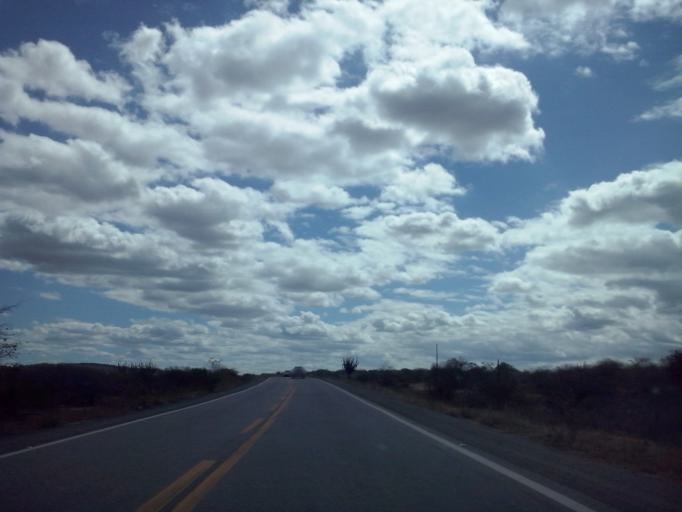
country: BR
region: Paraiba
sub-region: Soledade
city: Soledade
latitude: -7.0438
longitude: -36.3968
